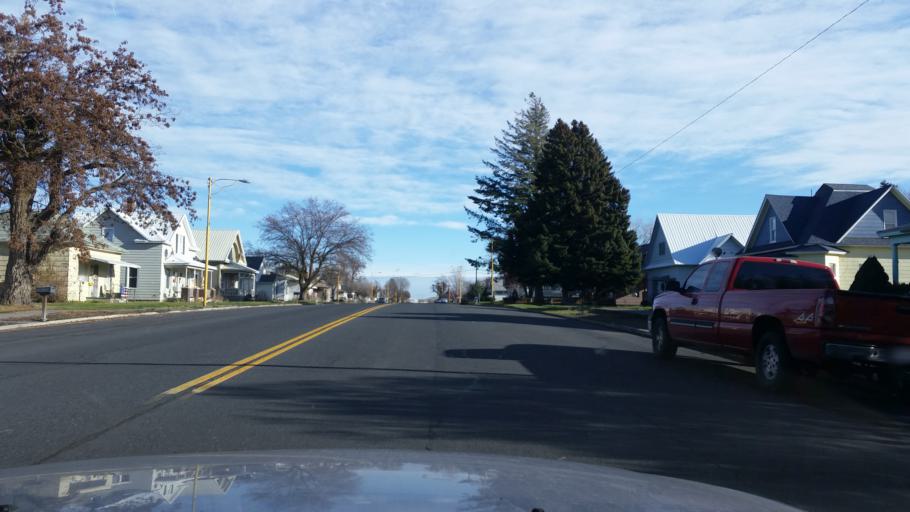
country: US
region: Washington
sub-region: Adams County
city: Ritzville
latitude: 47.3331
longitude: -118.6861
